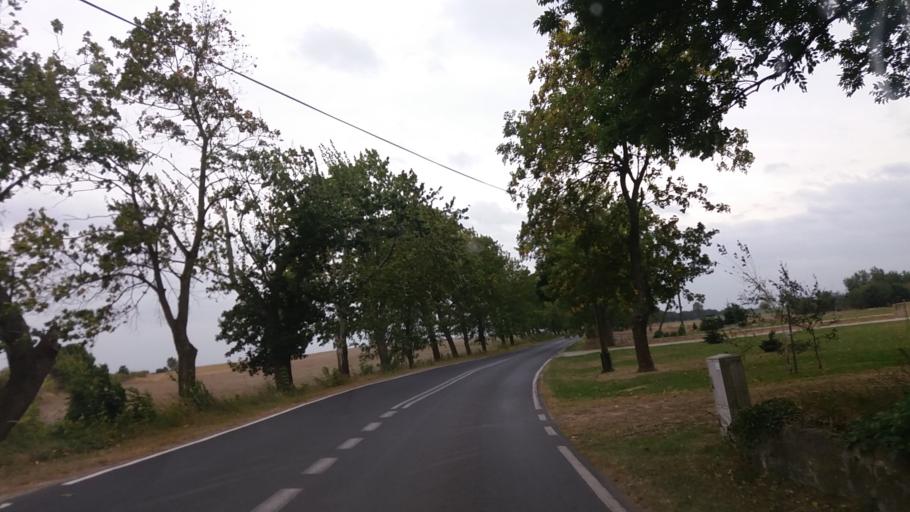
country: PL
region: Lubusz
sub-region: Powiat strzelecko-drezdenecki
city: Strzelce Krajenskie
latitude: 52.9240
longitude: 15.5637
